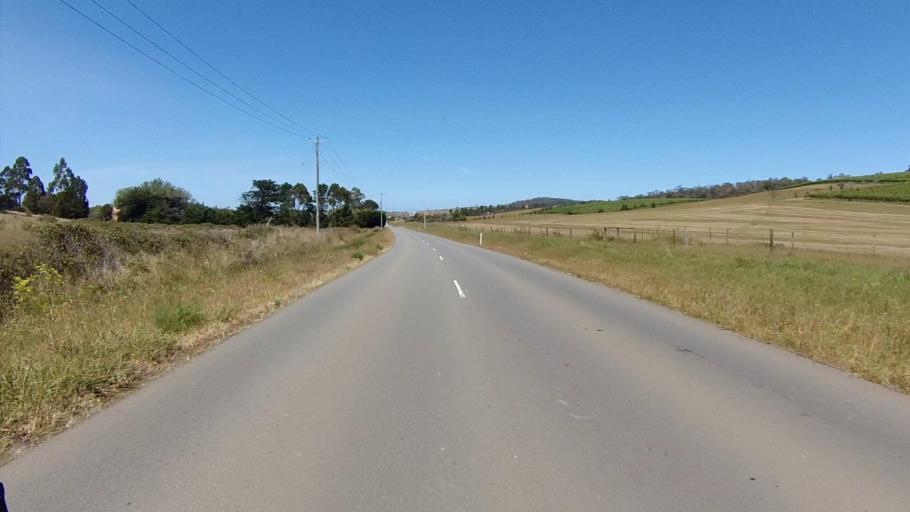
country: AU
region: Tasmania
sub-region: Clarence
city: Howrah
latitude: -42.8735
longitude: 147.4256
